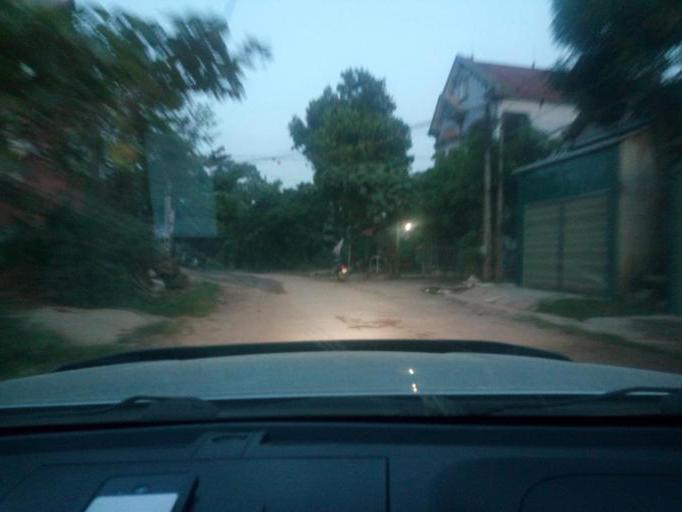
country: VN
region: Yen Bai
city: Co Phuc
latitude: 21.8612
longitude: 104.6336
